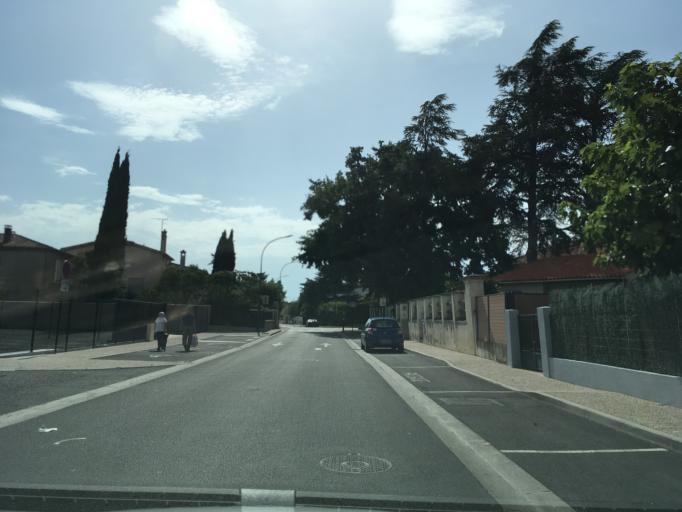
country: FR
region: Midi-Pyrenees
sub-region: Departement du Tarn
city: Castres
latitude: 43.6120
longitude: 2.2521
